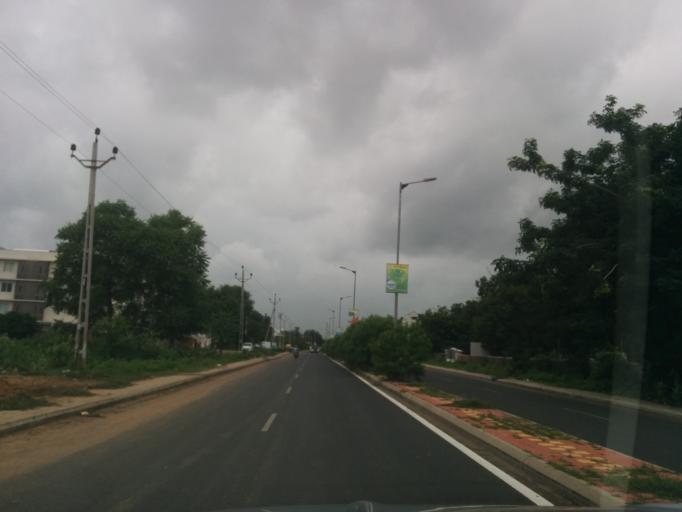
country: IN
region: Gujarat
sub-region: Ahmadabad
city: Sarkhej
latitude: 23.0520
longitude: 72.4853
